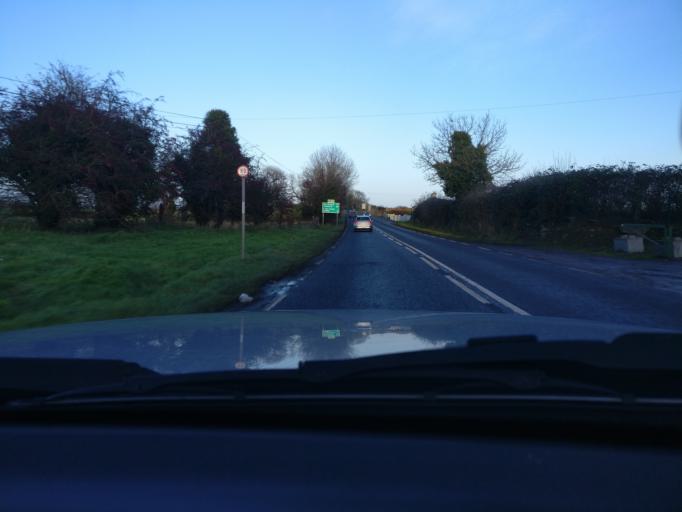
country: IE
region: Leinster
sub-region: Lu
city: Ardee
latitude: 53.8448
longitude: -6.6028
